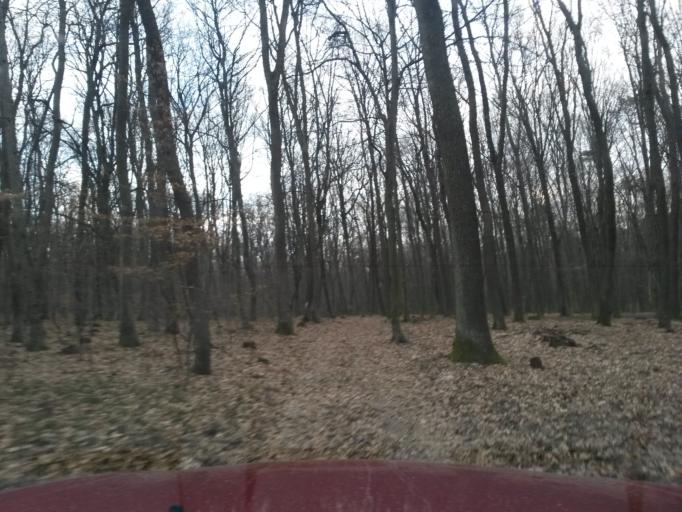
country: SK
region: Kosicky
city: Kosice
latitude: 48.6954
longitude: 21.3009
